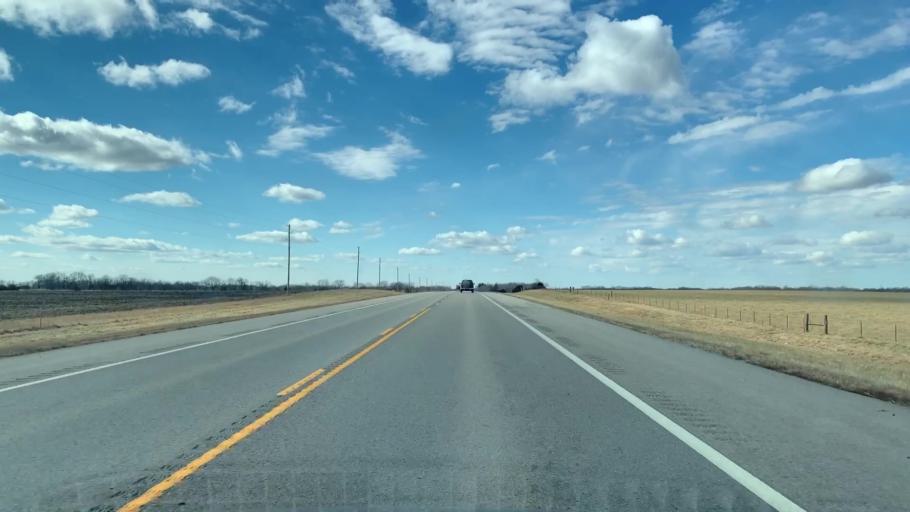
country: US
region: Kansas
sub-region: Labette County
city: Oswego
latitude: 37.3401
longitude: -95.0460
